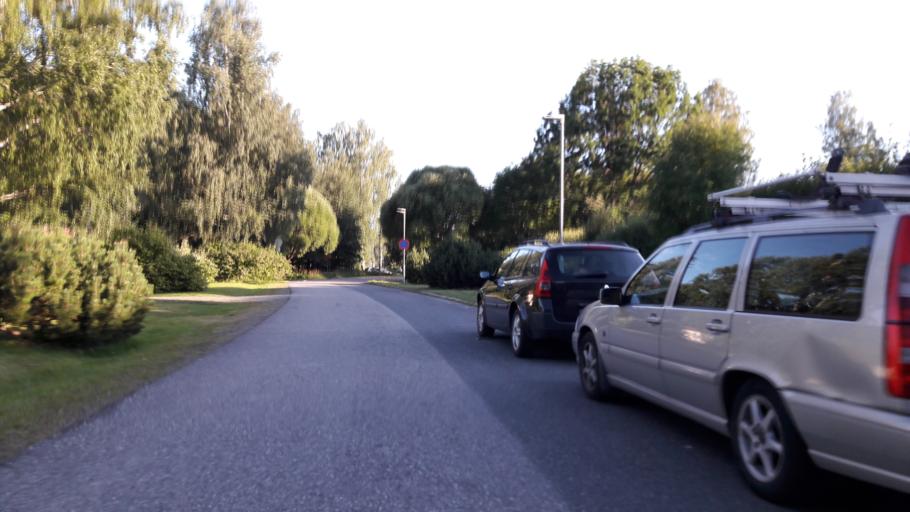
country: FI
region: North Karelia
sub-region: Joensuu
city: Joensuu
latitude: 62.6035
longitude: 29.7275
